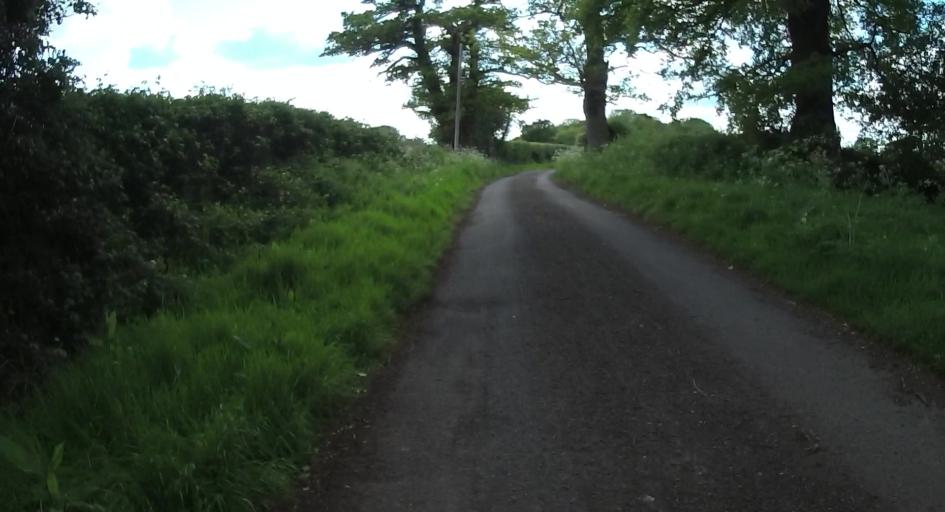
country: GB
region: England
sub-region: Wokingham
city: Swallowfield
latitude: 51.3628
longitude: -0.9753
